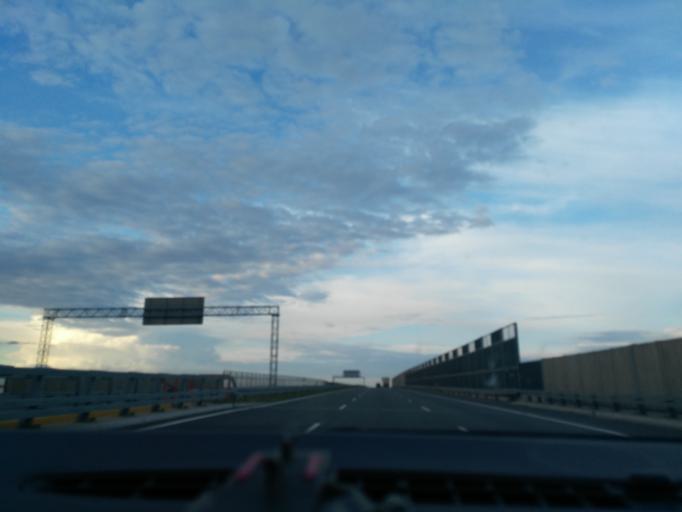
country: PL
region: Lublin Voivodeship
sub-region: Powiat lubelski
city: Jastkow
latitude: 51.2944
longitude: 22.4724
